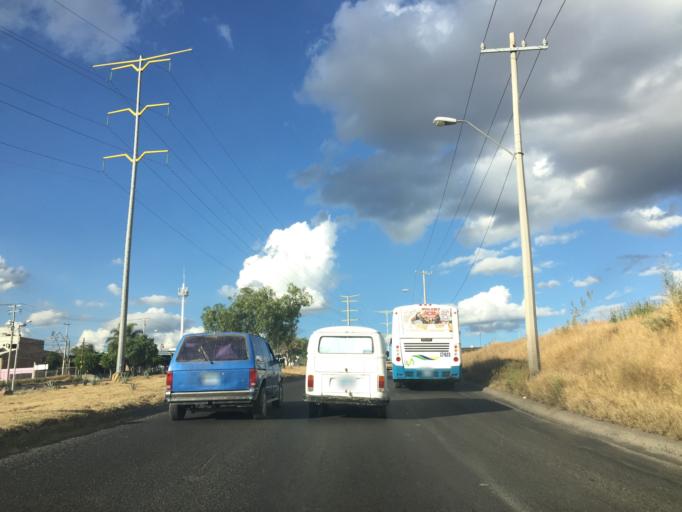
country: MX
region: Guanajuato
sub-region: Leon
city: Ejido la Joya
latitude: 21.1101
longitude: -101.7116
